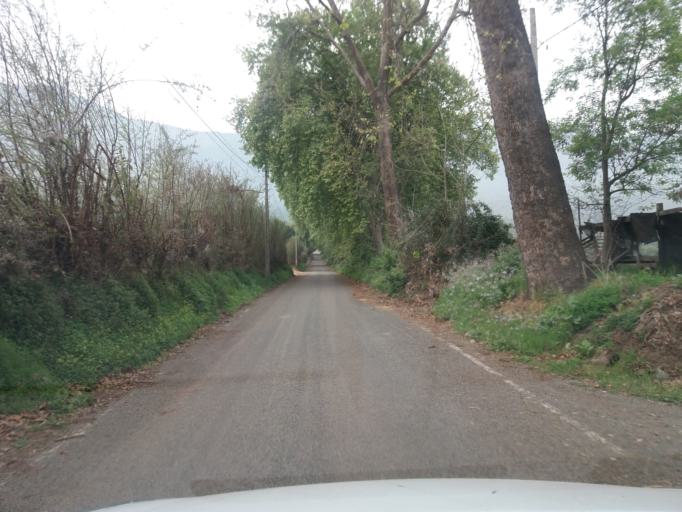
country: CL
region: Valparaiso
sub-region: Provincia de San Felipe
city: Llaillay
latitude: -32.8475
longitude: -71.0623
